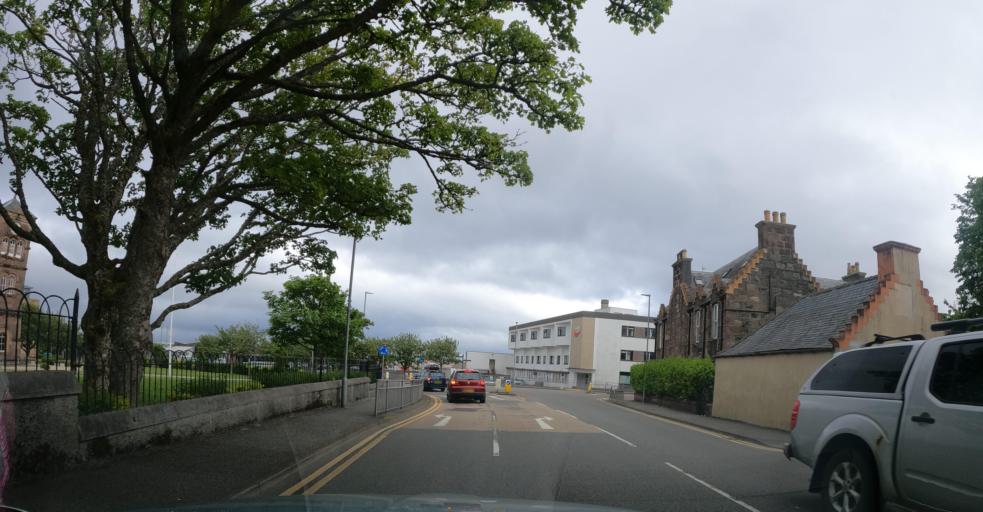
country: GB
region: Scotland
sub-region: Eilean Siar
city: Stornoway
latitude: 58.2089
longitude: -6.3816
